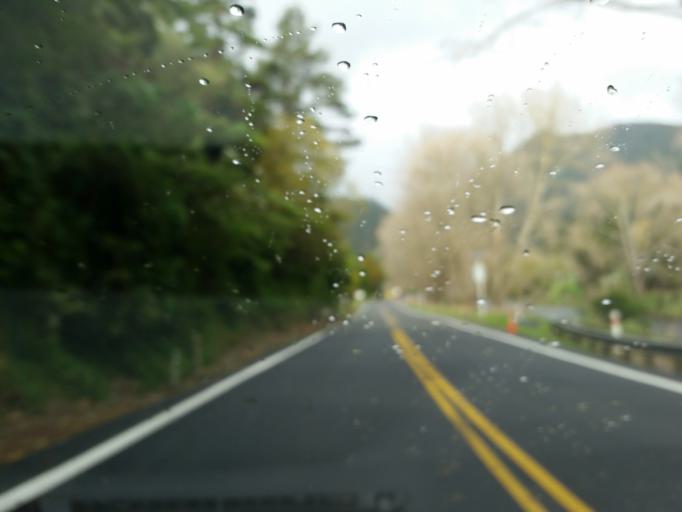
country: NZ
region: Waikato
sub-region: Hauraki District
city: Paeroa
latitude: -37.4133
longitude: 175.7145
